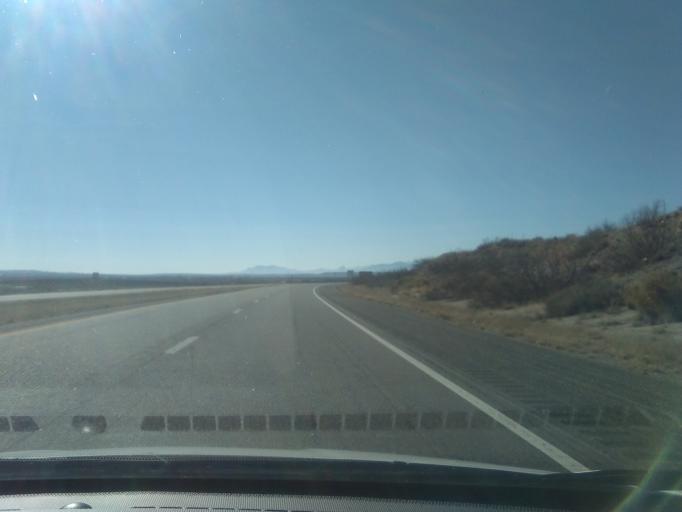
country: US
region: New Mexico
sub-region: Valencia County
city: Jarales
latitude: 34.4272
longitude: -106.8331
